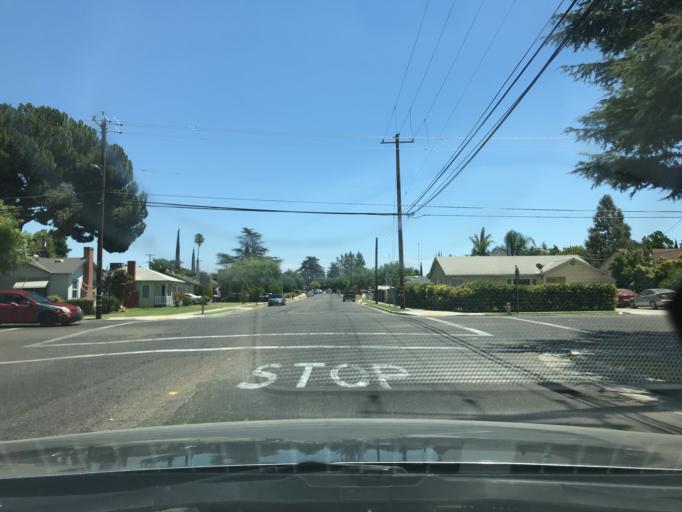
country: US
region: California
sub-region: Merced County
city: Atwater
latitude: 37.3534
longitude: -120.6055
